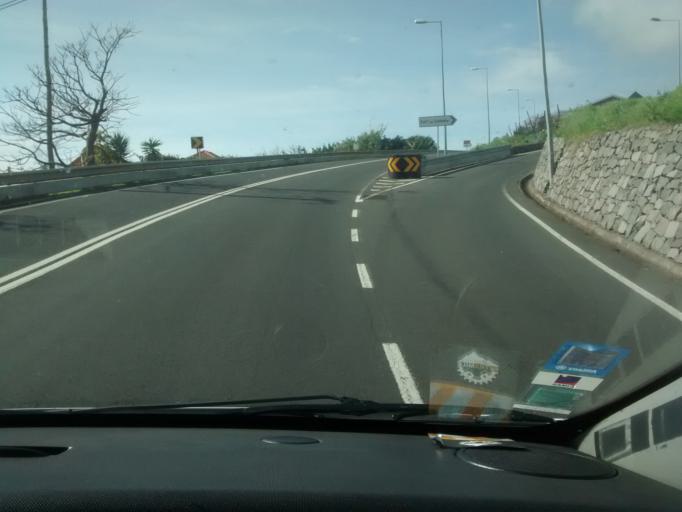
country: PT
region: Madeira
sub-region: Calheta
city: Estreito da Calheta
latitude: 32.7304
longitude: -17.1873
